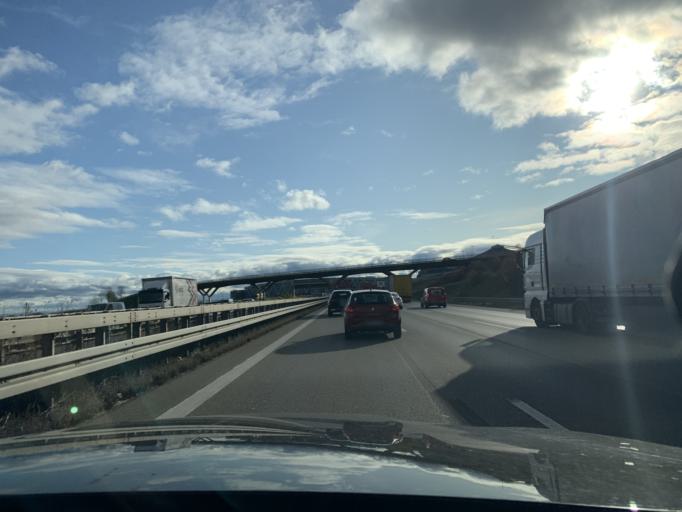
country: DE
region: Baden-Wuerttemberg
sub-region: Regierungsbezirk Stuttgart
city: Leinfelden-Echterdingen
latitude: 48.6990
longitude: 9.1850
